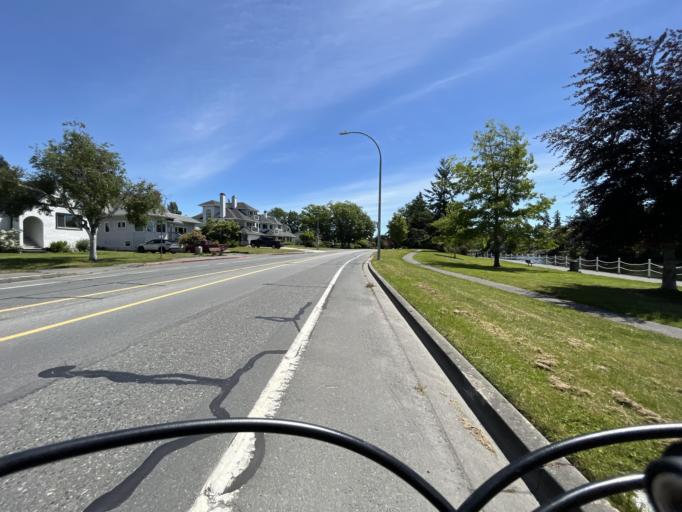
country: CA
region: British Columbia
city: Victoria
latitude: 48.4514
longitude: -123.4155
